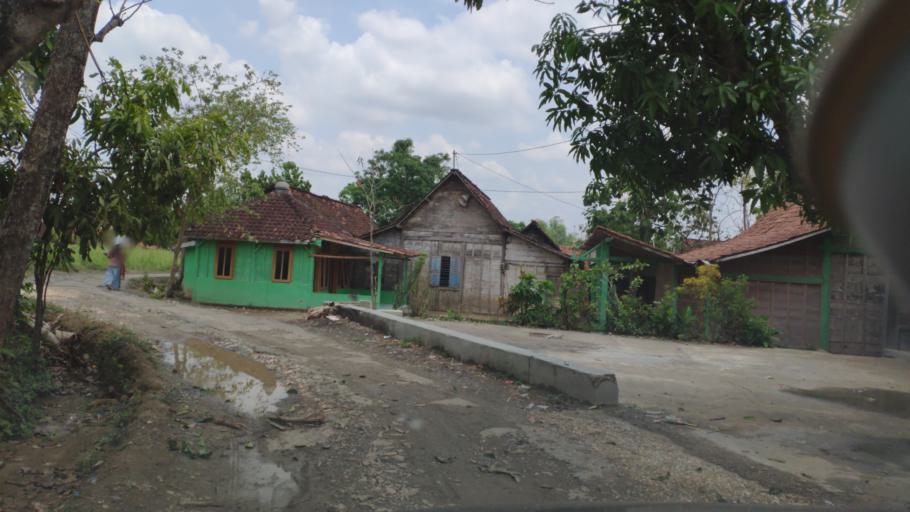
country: ID
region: Central Java
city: Gumiring
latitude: -7.0437
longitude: 111.3921
